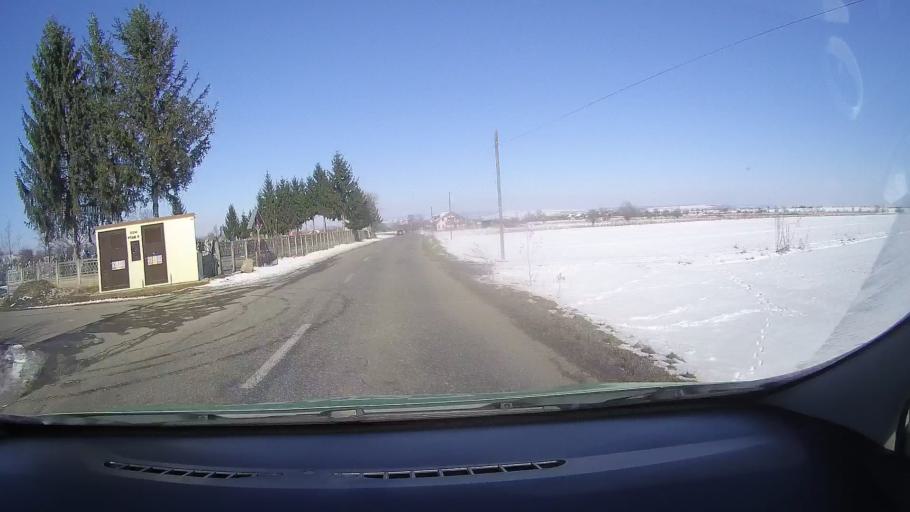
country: RO
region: Brasov
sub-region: Comuna Harseni
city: Harseni
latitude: 45.7813
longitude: 25.0014
